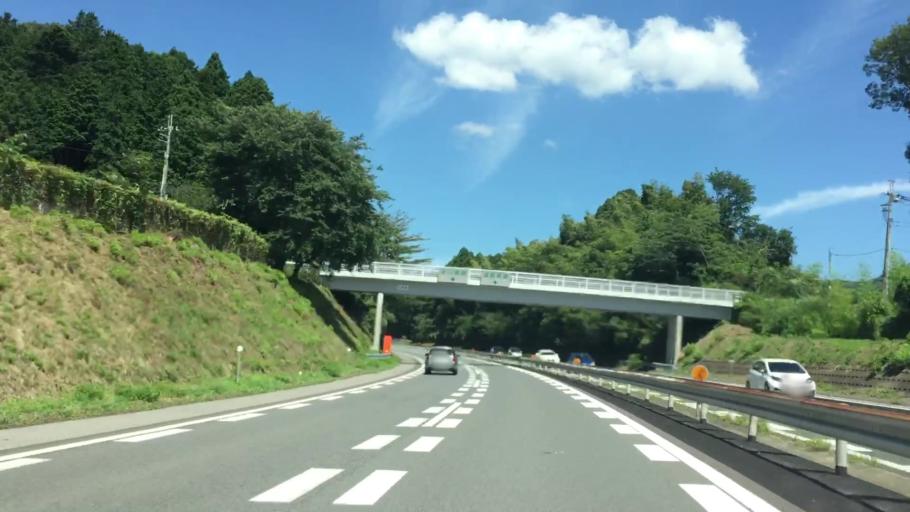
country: JP
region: Tochigi
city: Utsunomiya-shi
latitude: 36.6632
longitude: 139.8342
